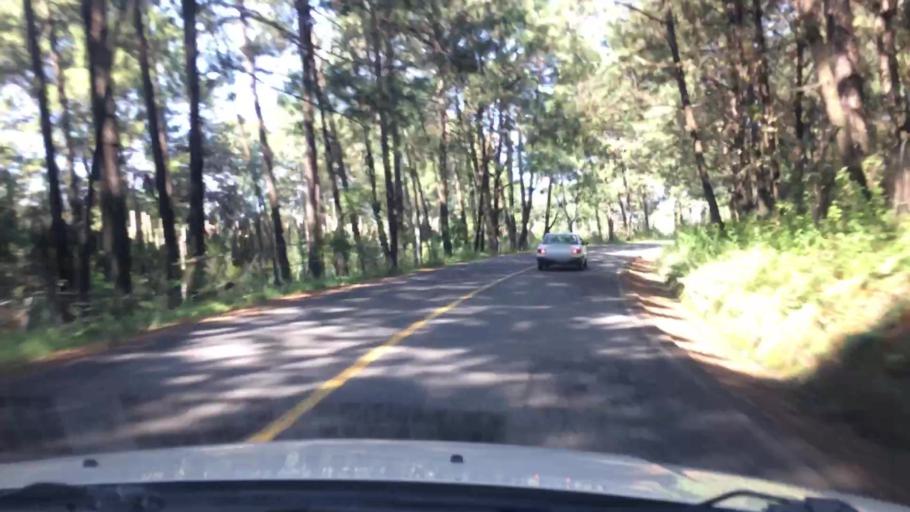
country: MX
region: Mexico
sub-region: Valle de Bravo
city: Casas Viejas
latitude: 19.1547
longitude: -100.0914
